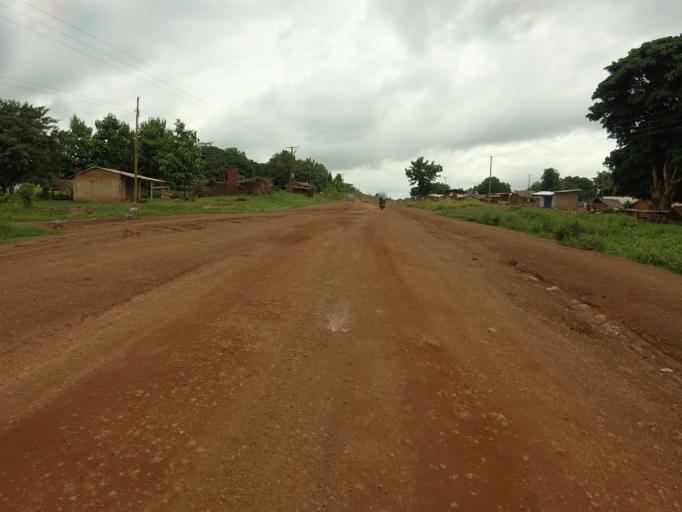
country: GH
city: Kpandae
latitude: 8.3128
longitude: 0.4815
